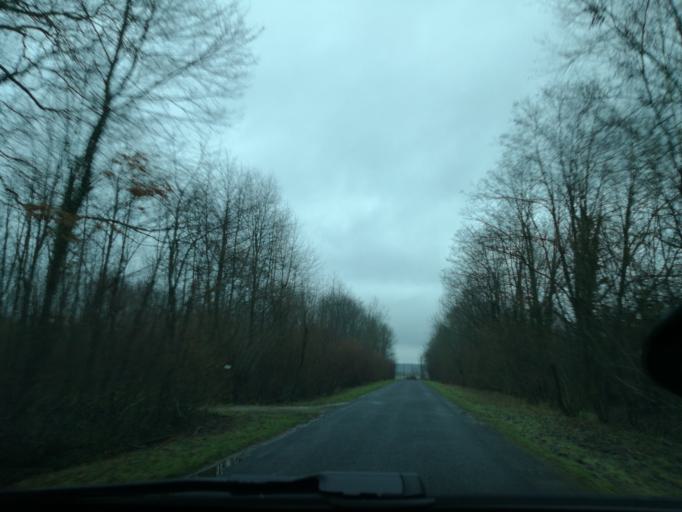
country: FR
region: Lorraine
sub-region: Departement de la Meuse
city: Revigny-sur-Ornain
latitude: 48.8590
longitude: 5.0698
